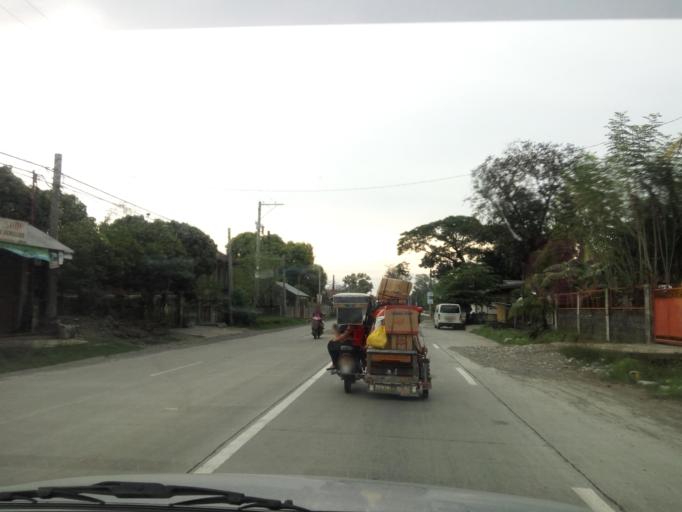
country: PH
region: Ilocos
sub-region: Province of Pangasinan
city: Bobonan
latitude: 16.1352
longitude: 120.5264
